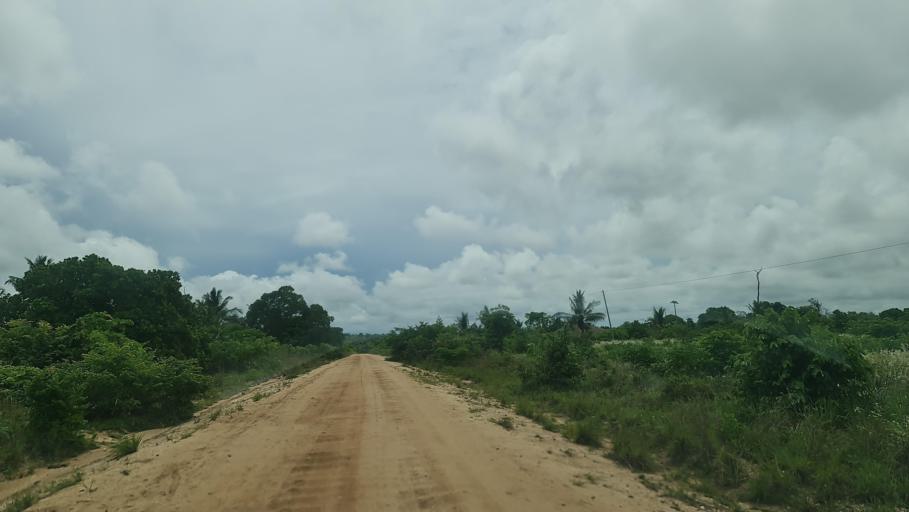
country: MZ
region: Zambezia
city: Quelimane
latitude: -17.2667
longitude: 37.2434
